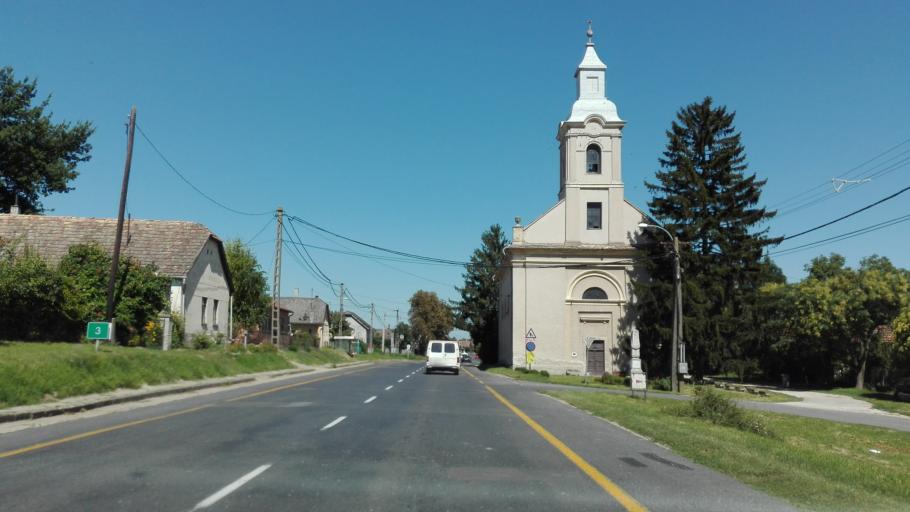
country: HU
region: Tolna
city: Simontornya
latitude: 46.7740
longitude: 18.5152
